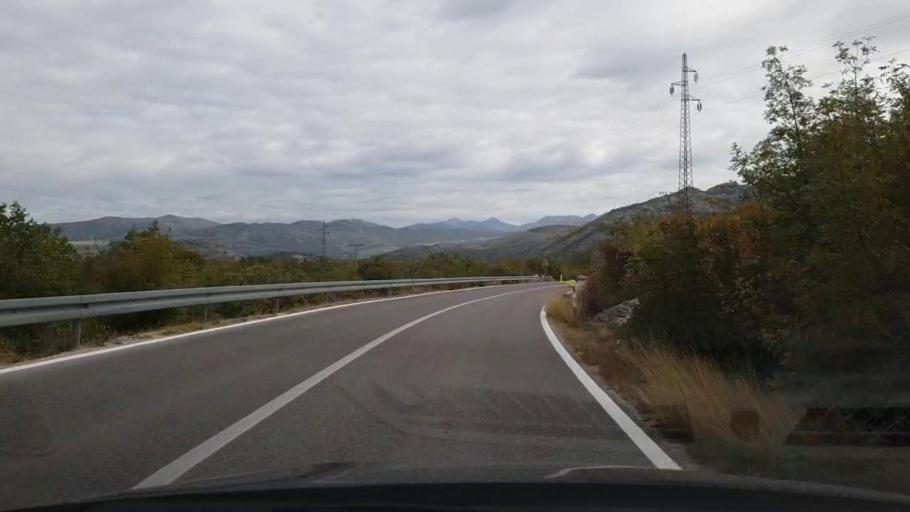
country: BA
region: Republika Srpska
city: Trebinje
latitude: 42.6905
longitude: 18.2745
